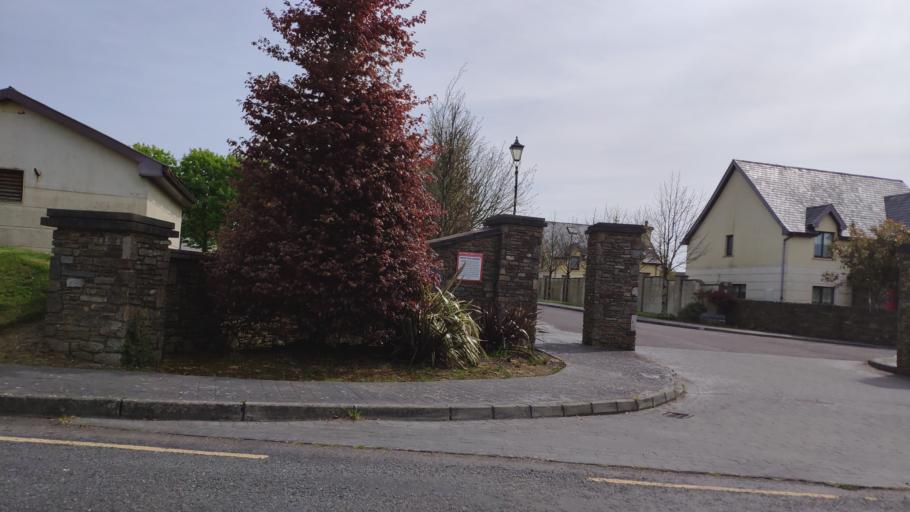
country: IE
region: Munster
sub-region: County Cork
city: Blarney
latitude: 51.9791
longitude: -8.5136
